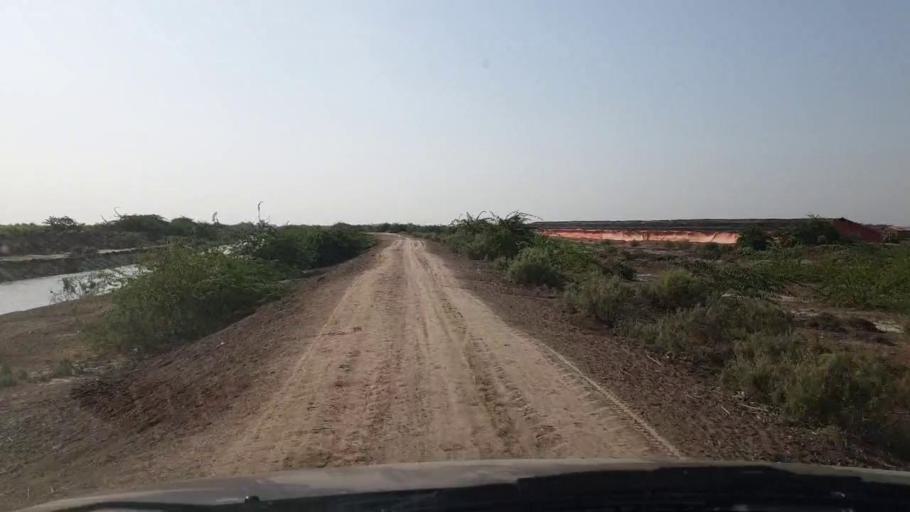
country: PK
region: Sindh
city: Kadhan
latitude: 24.6116
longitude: 69.0730
